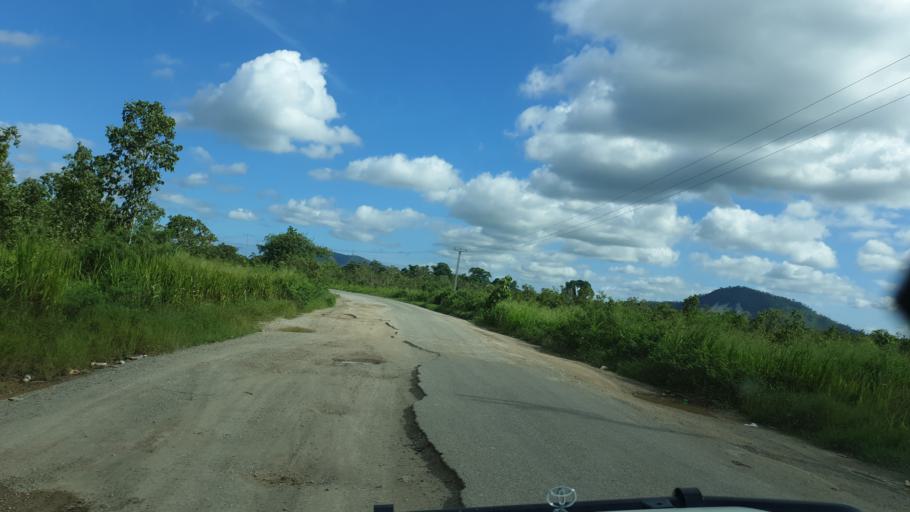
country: PG
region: National Capital
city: Port Moresby
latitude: -9.2582
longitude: 147.2291
